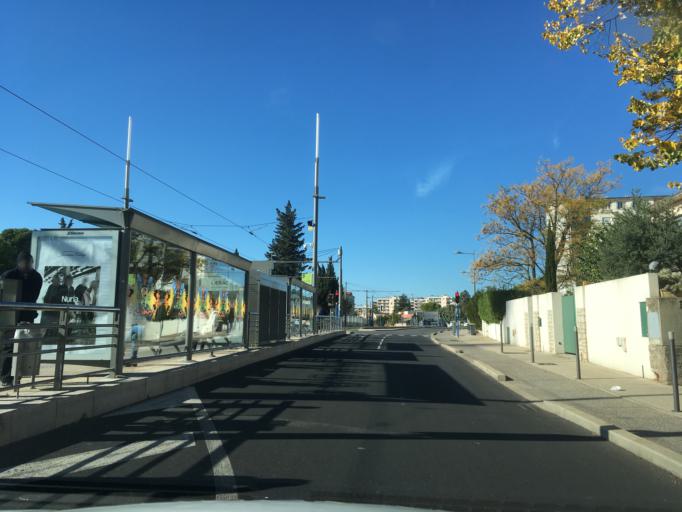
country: FR
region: Languedoc-Roussillon
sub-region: Departement de l'Herault
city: Montpellier
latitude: 43.6113
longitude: 3.8470
